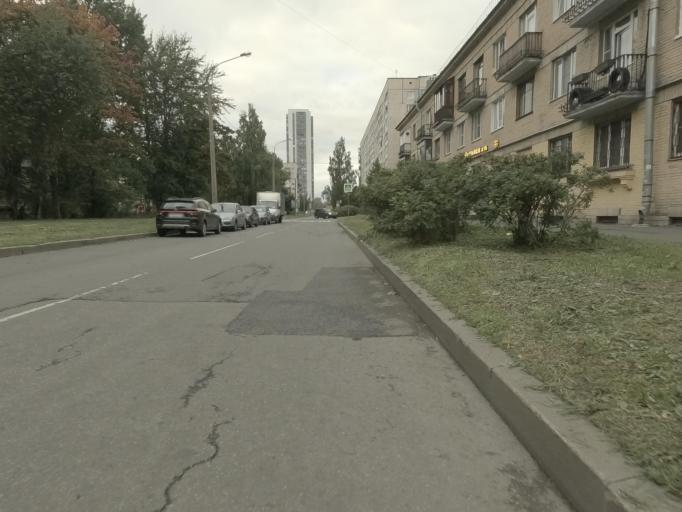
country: RU
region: St.-Petersburg
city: Krasnogvargeisky
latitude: 59.9576
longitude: 30.4851
